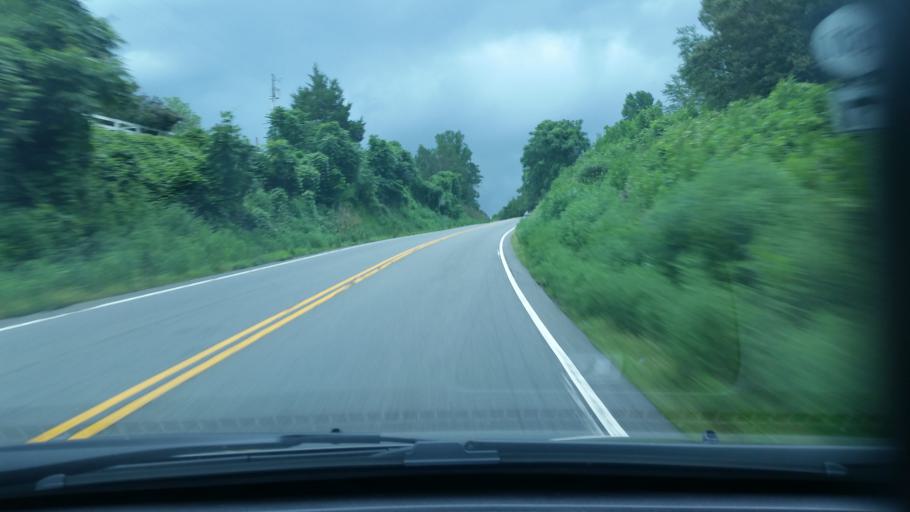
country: US
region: Virginia
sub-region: Nelson County
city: Nellysford
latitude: 37.8785
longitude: -78.8218
